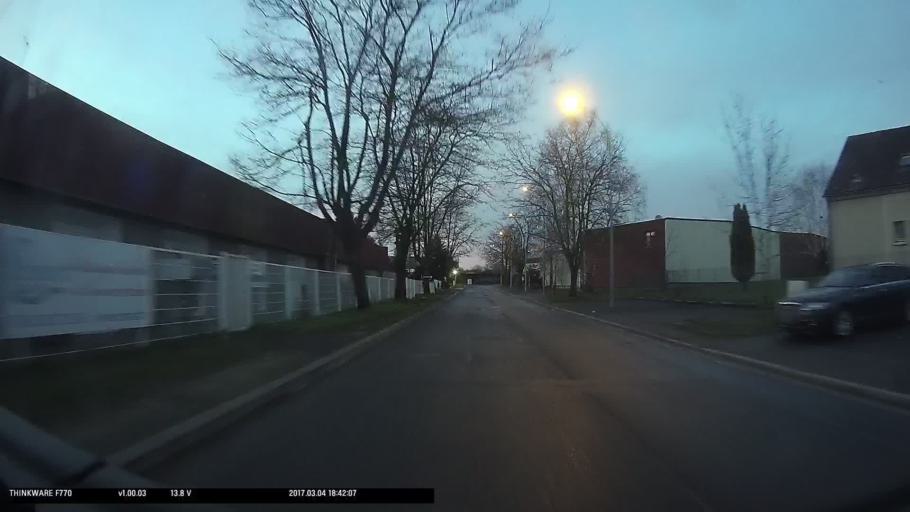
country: FR
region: Ile-de-France
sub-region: Departement du Val-d'Oise
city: Marines
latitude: 49.1464
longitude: 1.9686
